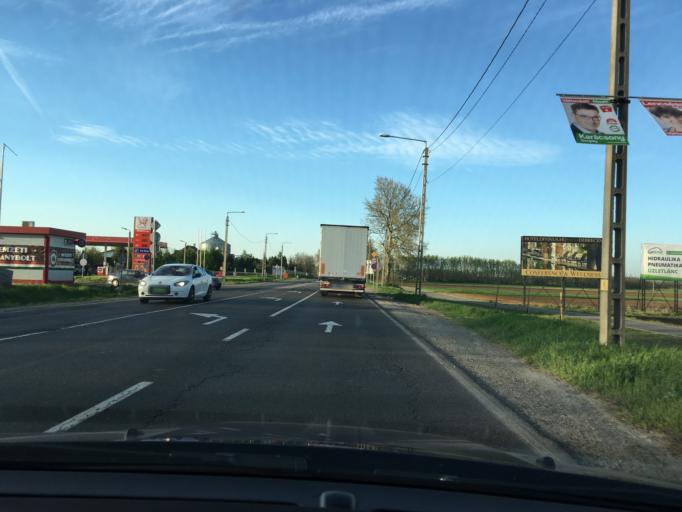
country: HU
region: Hajdu-Bihar
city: Mikepercs
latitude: 47.4521
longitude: 21.6337
